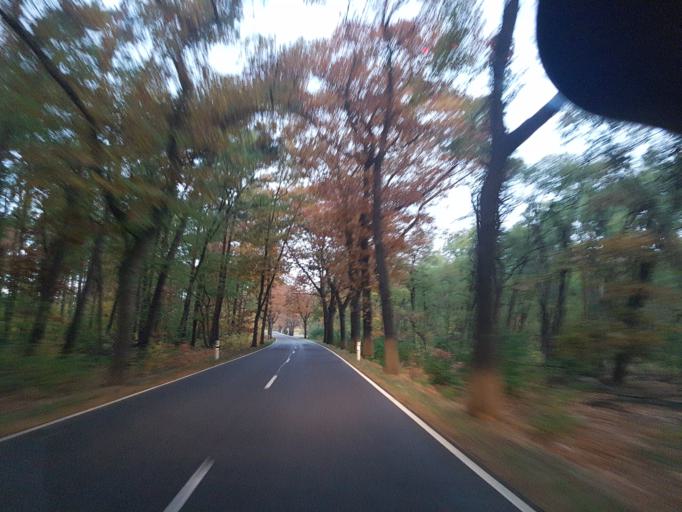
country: DE
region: Brandenburg
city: Ludwigsfelde
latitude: 52.2707
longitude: 13.2213
